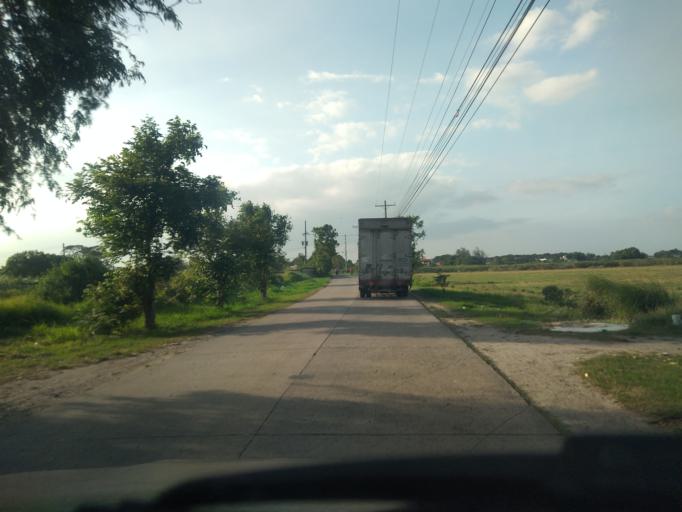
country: PH
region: Central Luzon
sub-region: Province of Pampanga
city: Malino
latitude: 15.1100
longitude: 120.6681
